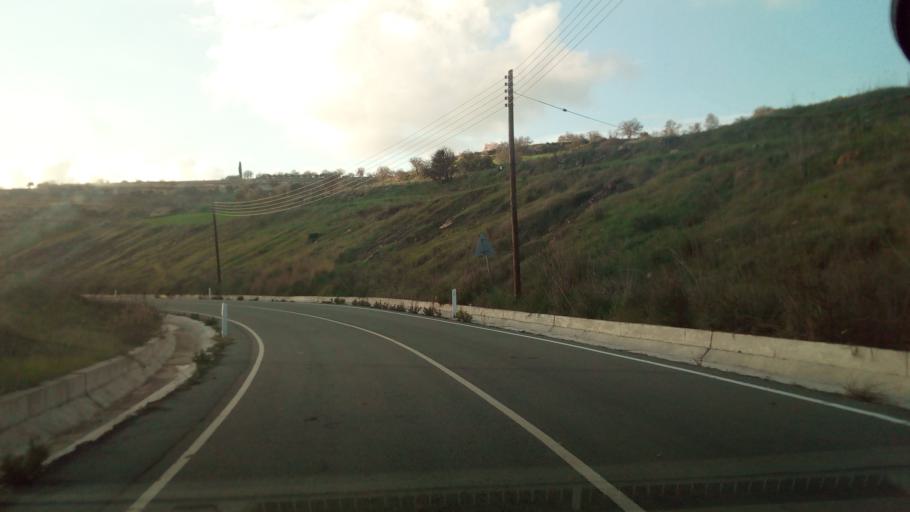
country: CY
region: Pafos
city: Mesogi
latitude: 34.9190
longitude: 32.5366
